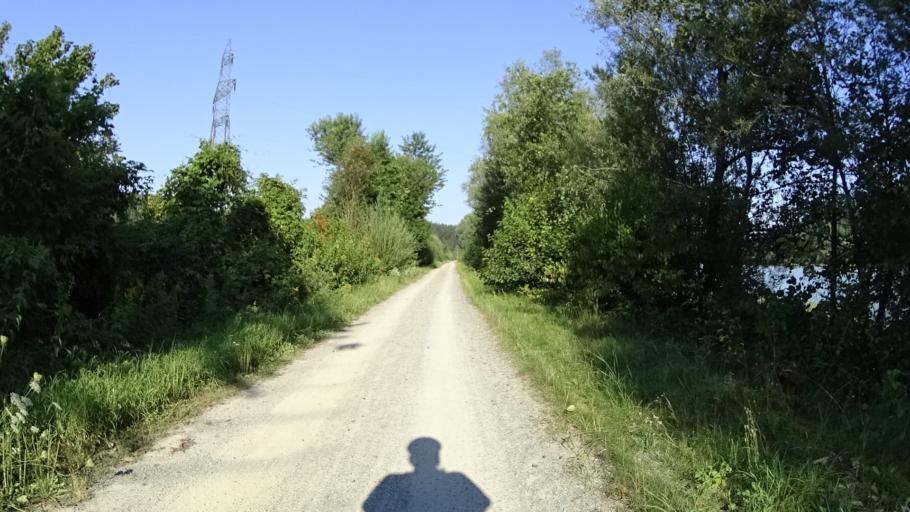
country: AT
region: Carinthia
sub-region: Politischer Bezirk Villach Land
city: Wernberg
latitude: 46.5944
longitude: 13.9735
